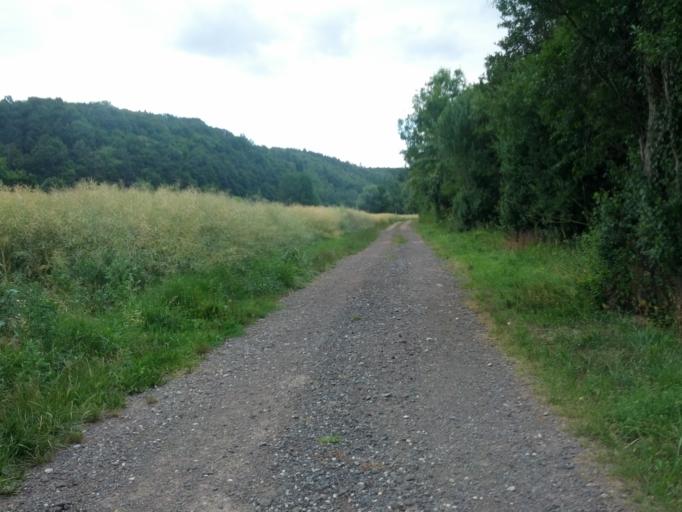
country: DE
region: Thuringia
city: Krauthausen
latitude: 50.9903
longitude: 10.2537
